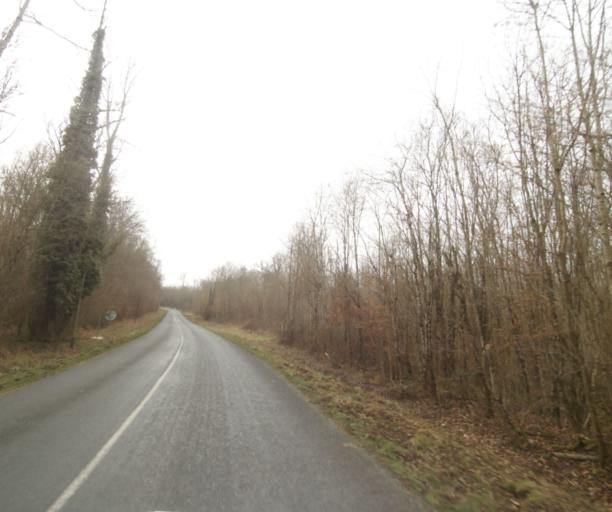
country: FR
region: Champagne-Ardenne
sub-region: Departement de la Haute-Marne
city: Villiers-en-Lieu
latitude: 48.6971
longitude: 4.8948
